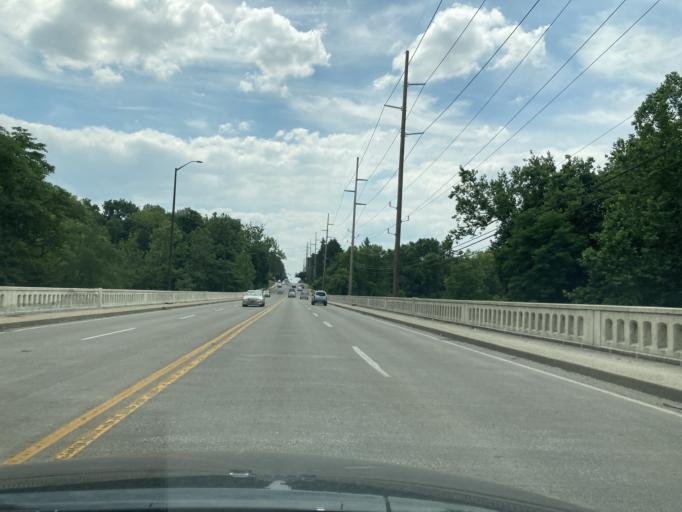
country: US
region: Indiana
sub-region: Marion County
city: Broad Ripple
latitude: 39.8329
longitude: -86.1848
